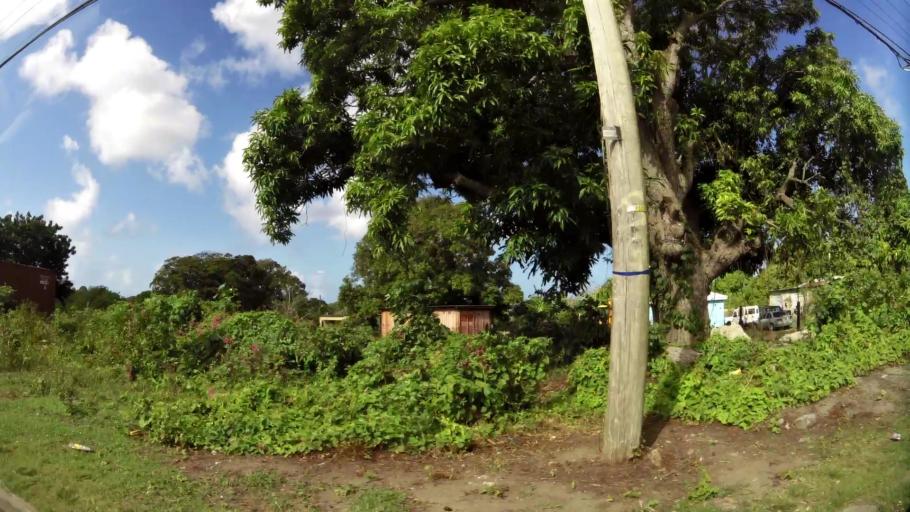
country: KN
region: Saint Paul Charlestown
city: Charlestown
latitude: 17.1335
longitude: -62.6186
